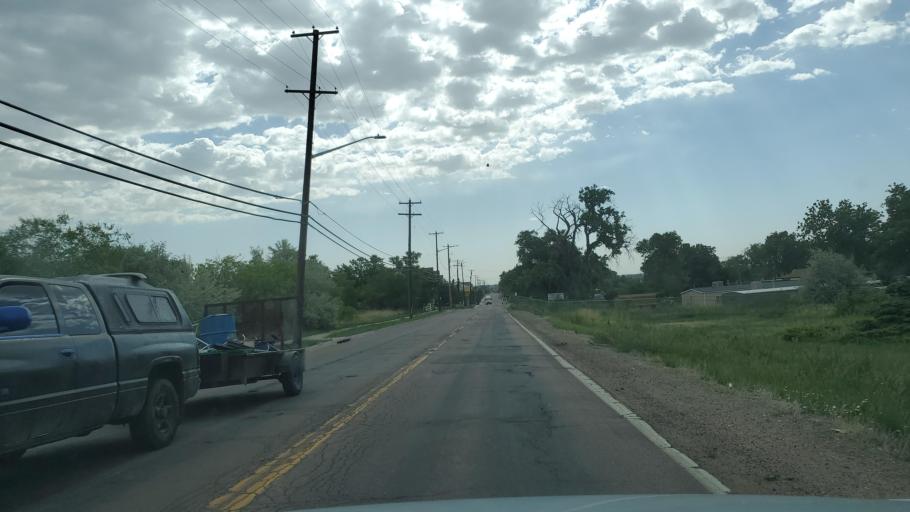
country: US
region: Colorado
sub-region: Adams County
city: Welby
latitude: 39.8381
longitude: -104.9698
